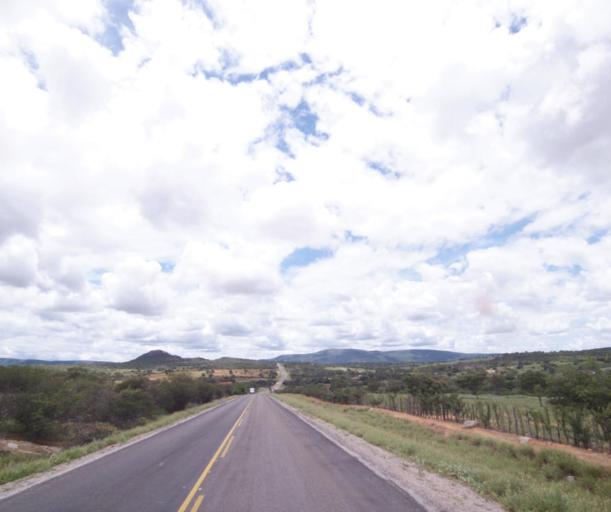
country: BR
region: Bahia
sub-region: Brumado
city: Brumado
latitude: -14.1504
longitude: -41.4896
